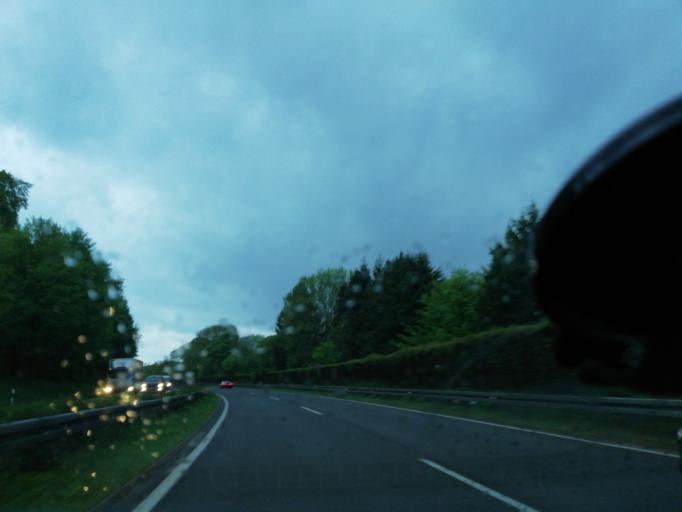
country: DE
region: North Rhine-Westphalia
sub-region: Regierungsbezirk Dusseldorf
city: Wuppertal
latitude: 51.2427
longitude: 7.1753
